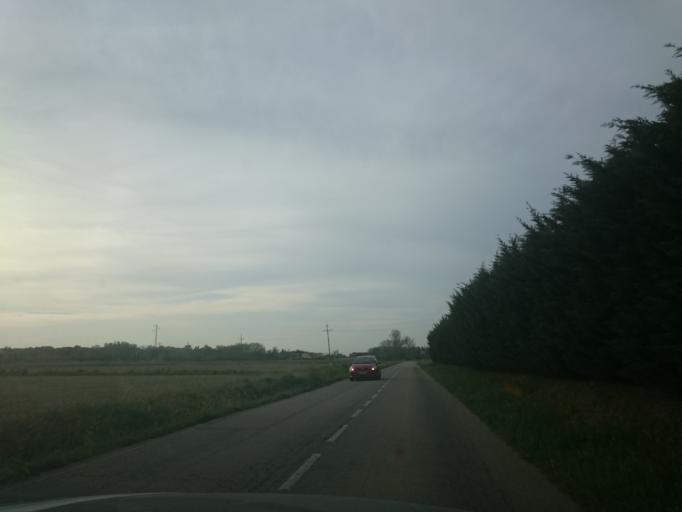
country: ES
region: Catalonia
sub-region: Provincia de Girona
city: Torroella de Montgri
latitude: 42.0176
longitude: 3.1466
